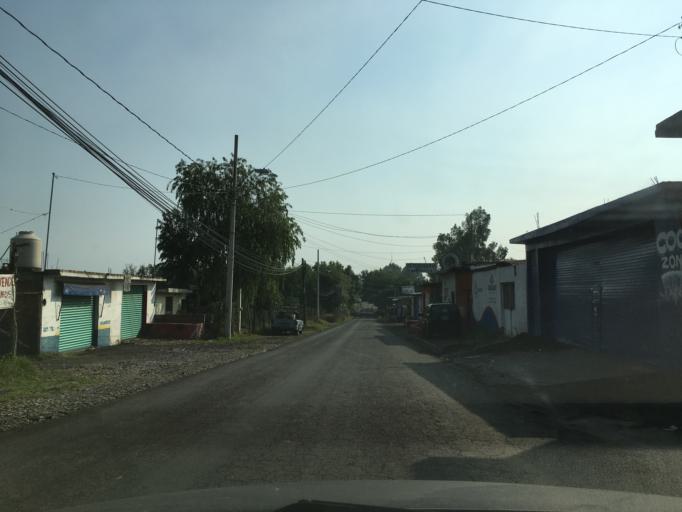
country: MX
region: Michoacan
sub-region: Morelia
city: Morelos
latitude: 19.6469
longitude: -101.2494
